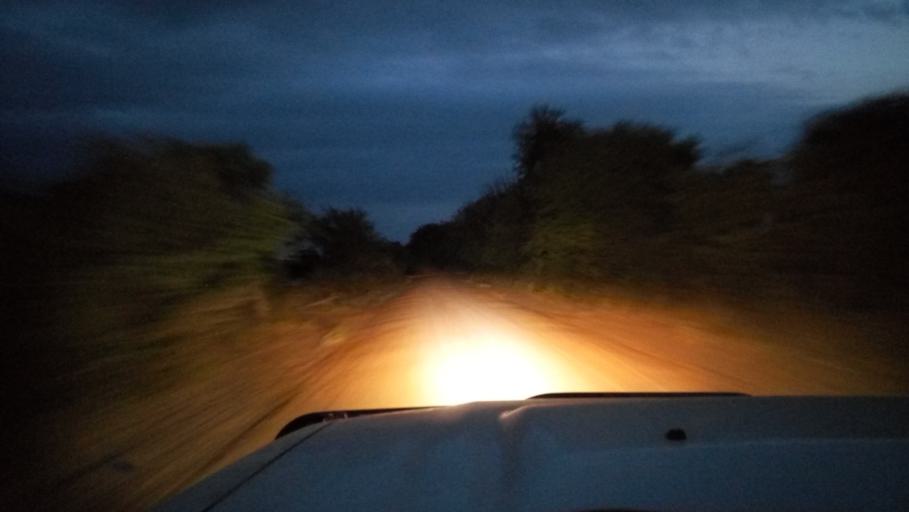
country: KE
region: Kitui
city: Kitui
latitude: -1.8257
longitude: 38.1989
